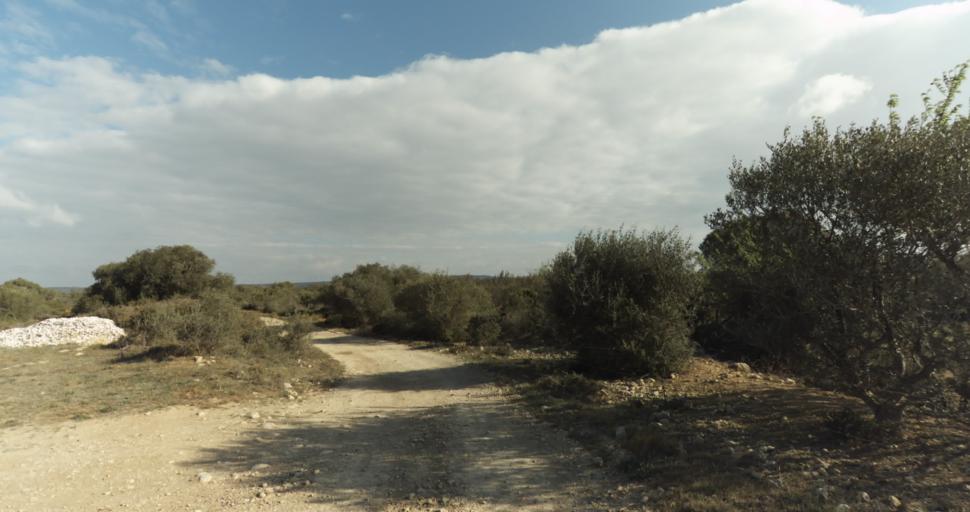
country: FR
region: Languedoc-Roussillon
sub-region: Departement de l'Aude
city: Leucate
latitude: 42.9381
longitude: 3.0122
